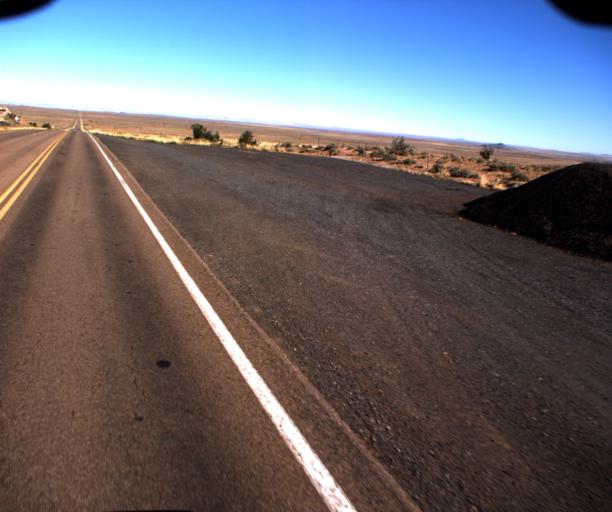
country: US
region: Arizona
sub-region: Navajo County
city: Snowflake
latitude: 34.6896
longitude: -110.1058
